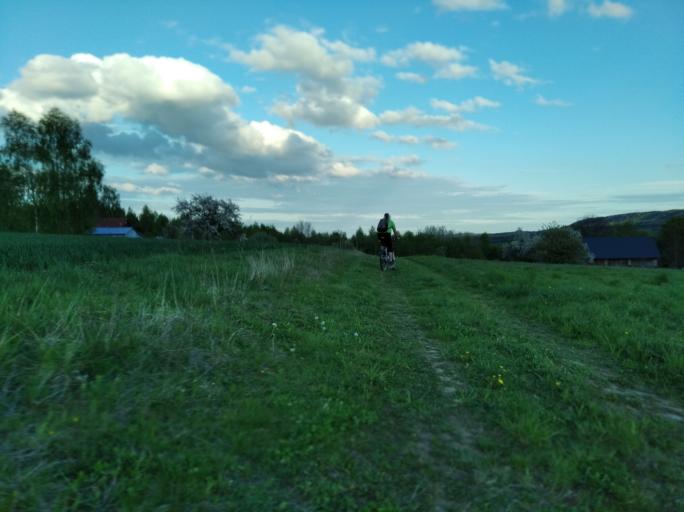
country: PL
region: Subcarpathian Voivodeship
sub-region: Powiat strzyzowski
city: Wysoka Strzyzowska
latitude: 49.8541
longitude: 21.7644
